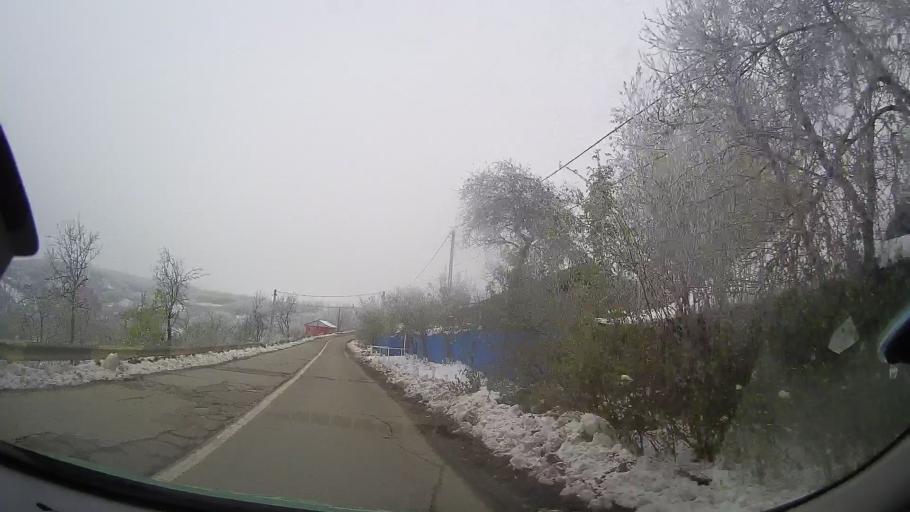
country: RO
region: Vaslui
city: Coroiesti
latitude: 46.2157
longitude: 27.4406
